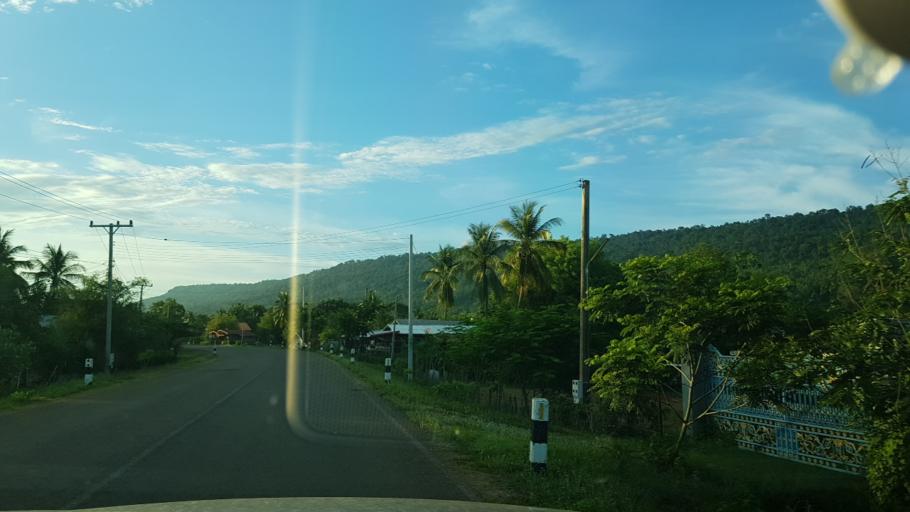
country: TH
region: Nong Khai
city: Sangkhom
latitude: 18.1372
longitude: 102.2821
